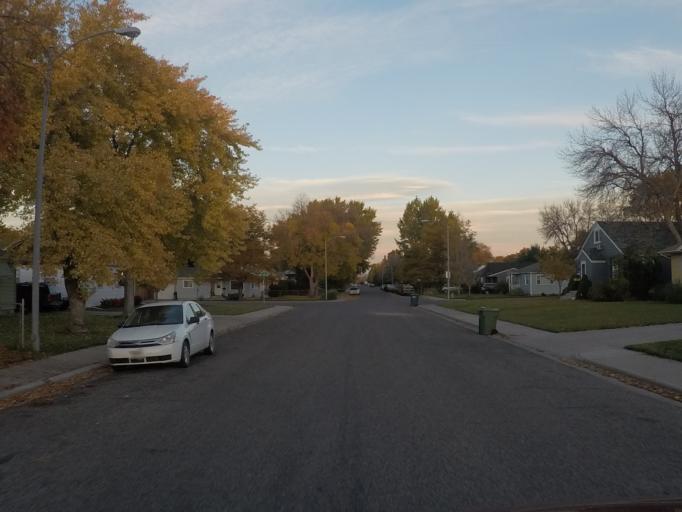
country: US
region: Montana
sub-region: Yellowstone County
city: Billings
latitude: 45.7879
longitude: -108.5468
